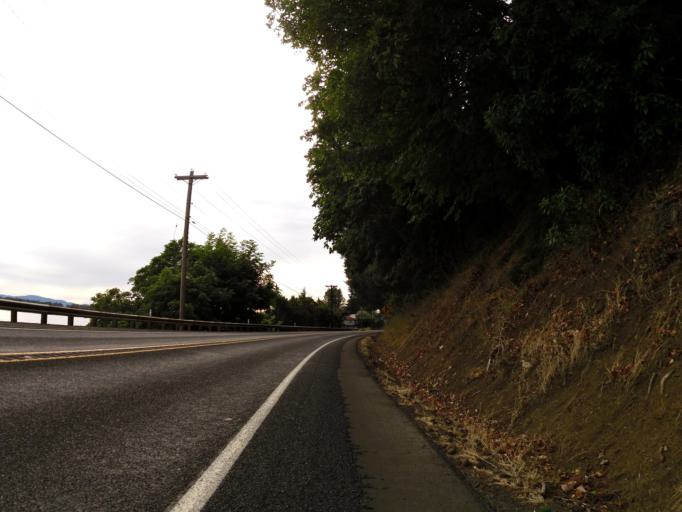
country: US
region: Washington
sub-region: Cowlitz County
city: West Longview
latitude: 46.1899
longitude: -123.1168
